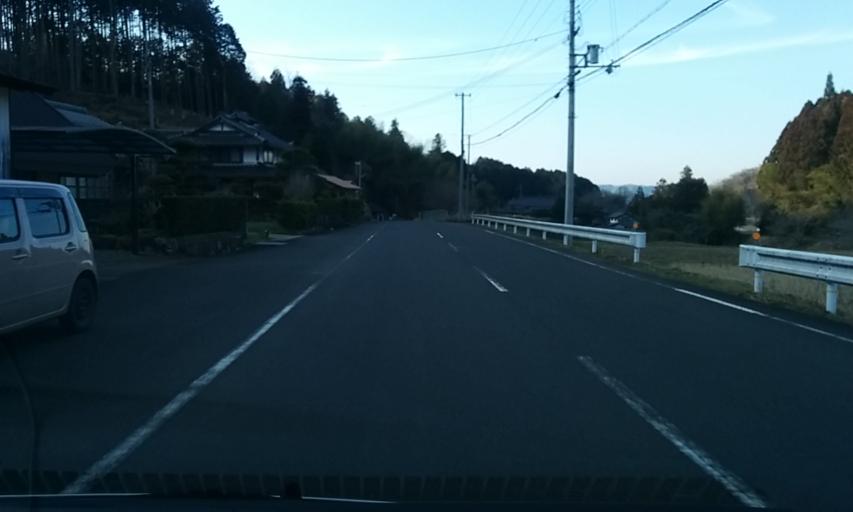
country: JP
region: Kyoto
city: Ayabe
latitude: 35.2844
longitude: 135.2388
